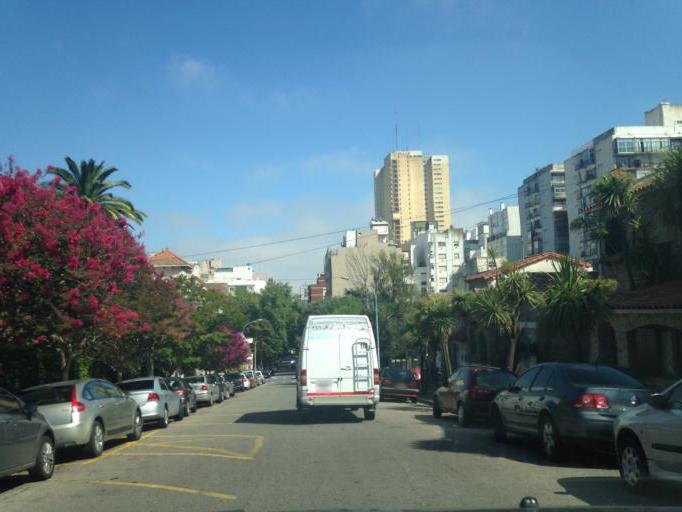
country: AR
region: Buenos Aires
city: Mar del Plata
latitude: -38.0114
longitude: -57.5369
